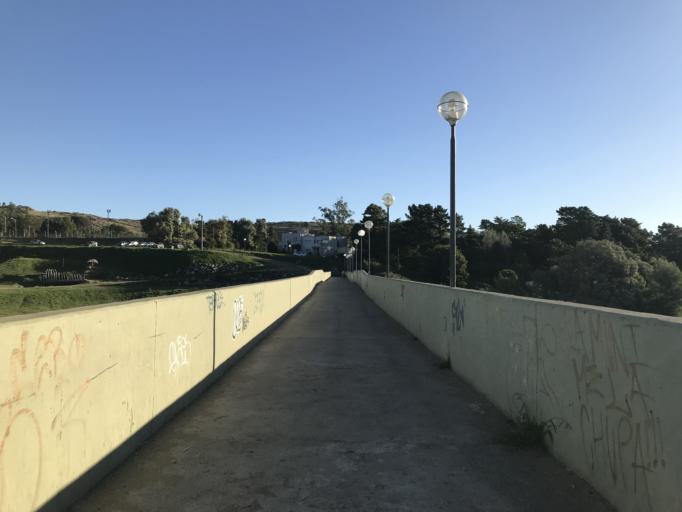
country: AR
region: Buenos Aires
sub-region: Partido de Tandil
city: Tandil
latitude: -37.3371
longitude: -59.1141
